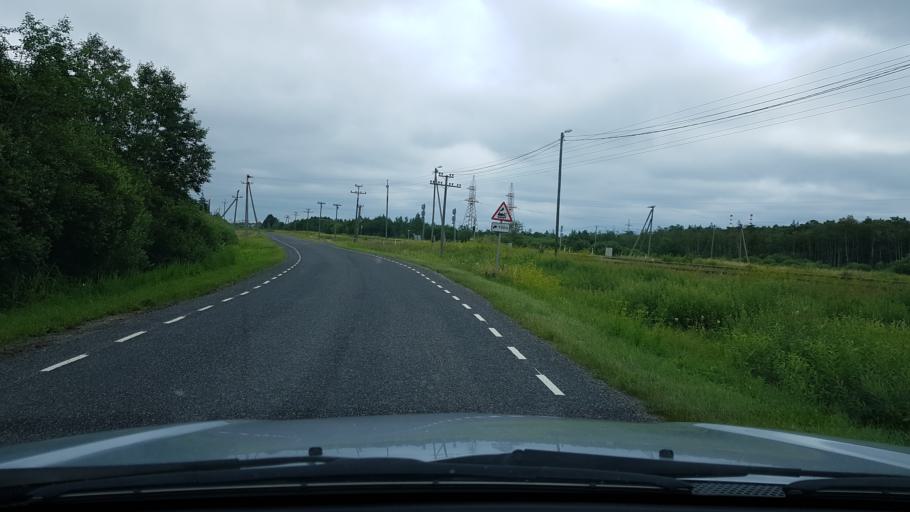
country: EE
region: Ida-Virumaa
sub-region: Narva-Joesuu linn
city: Narva-Joesuu
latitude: 59.3759
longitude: 28.0718
